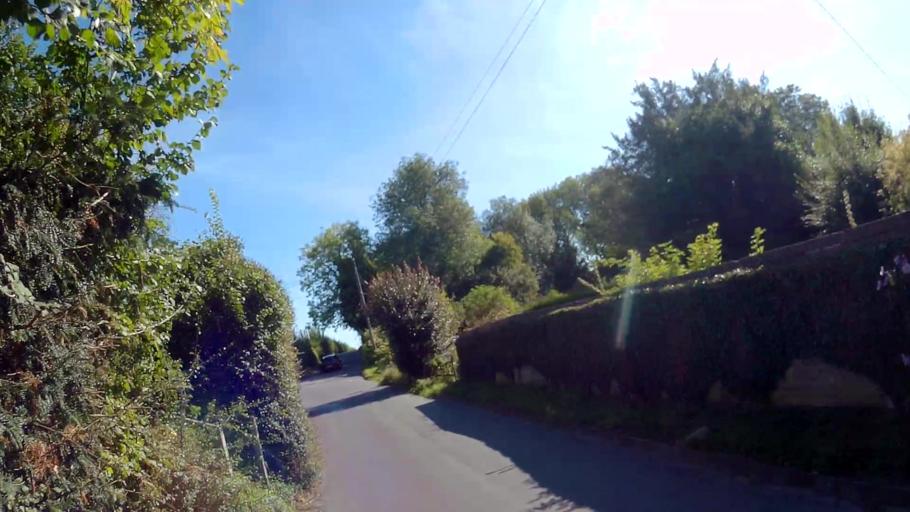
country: GB
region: England
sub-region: Hampshire
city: Andover
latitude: 51.1582
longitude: -1.4345
